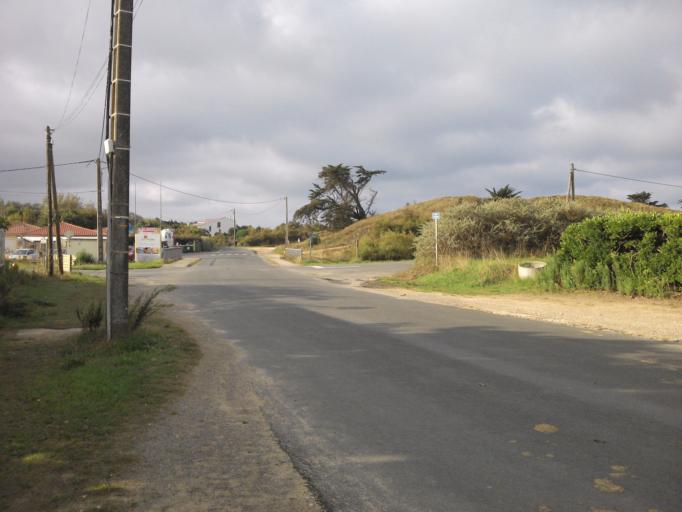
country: FR
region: Poitou-Charentes
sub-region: Departement de la Charente-Maritime
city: Saint-Denis-d'Oleron
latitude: 46.0159
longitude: -1.3926
